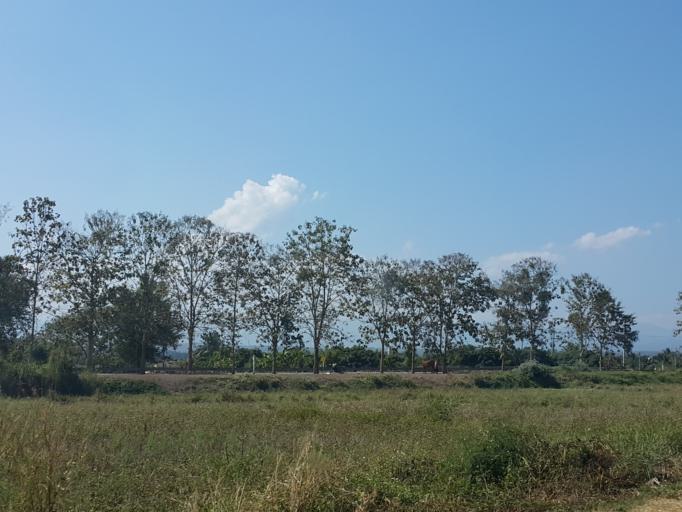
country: TH
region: Chiang Mai
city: Mae Taeng
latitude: 19.0342
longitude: 98.9820
